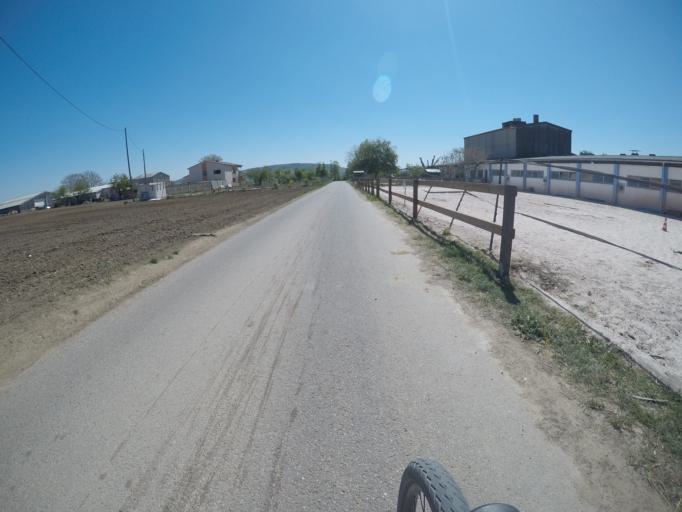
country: DE
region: Baden-Wuerttemberg
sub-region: Regierungsbezirk Stuttgart
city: Fellbach
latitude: 48.8375
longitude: 9.2759
